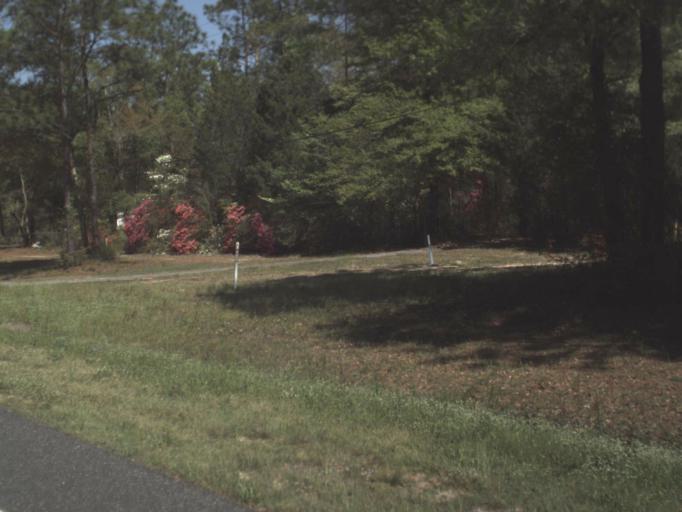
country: US
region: Florida
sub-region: Okaloosa County
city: Crestview
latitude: 30.7583
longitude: -86.6100
